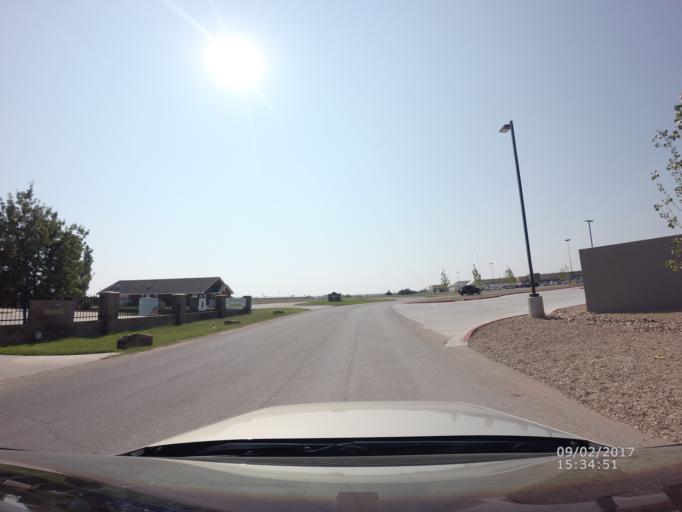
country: US
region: New Mexico
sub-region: Curry County
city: Clovis
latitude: 34.4364
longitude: -103.1972
